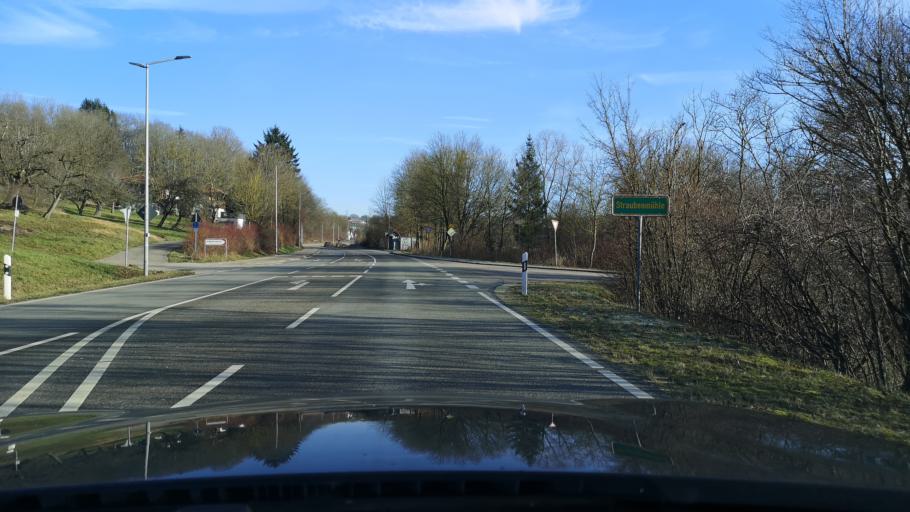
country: DE
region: Baden-Wuerttemberg
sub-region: Regierungsbezirk Stuttgart
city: Huttlingen
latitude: 48.8936
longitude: 10.0870
